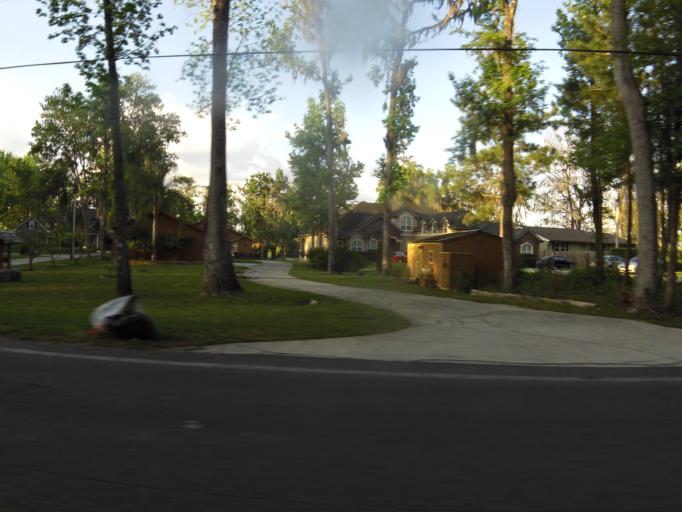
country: US
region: Florida
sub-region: Saint Johns County
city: Fruit Cove
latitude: 30.1248
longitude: -81.5931
